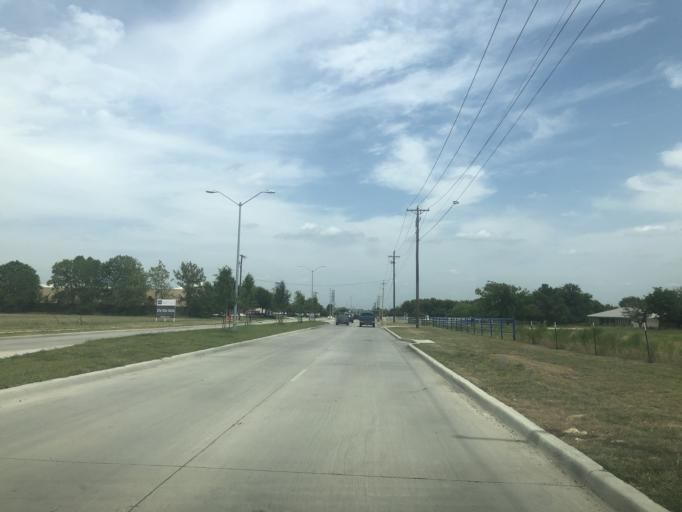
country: US
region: Texas
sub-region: Tarrant County
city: Saginaw
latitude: 32.8837
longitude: -97.3597
